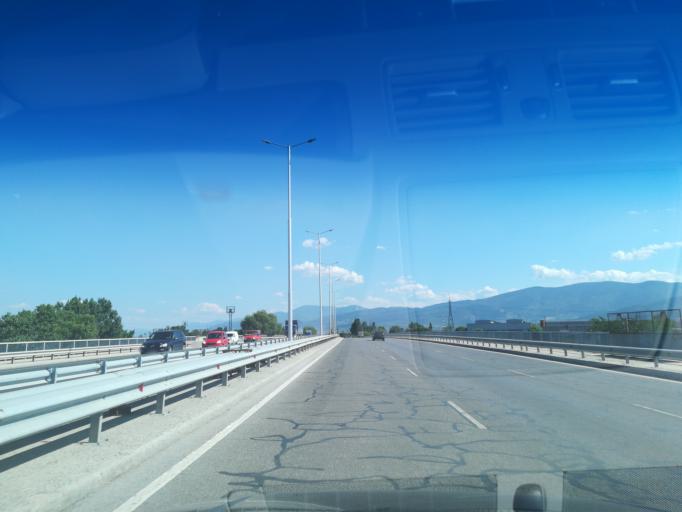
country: BG
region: Plovdiv
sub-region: Obshtina Plovdiv
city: Plovdiv
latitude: 42.1177
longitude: 24.7765
